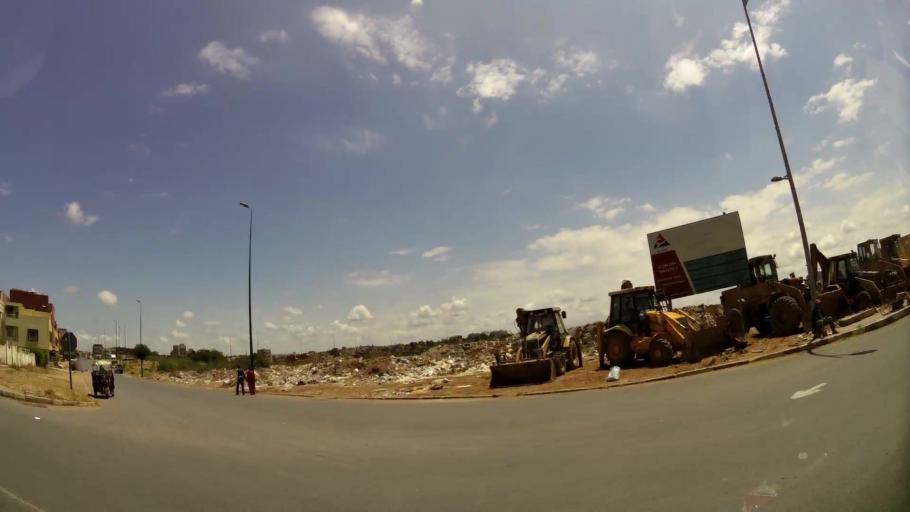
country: MA
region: Gharb-Chrarda-Beni Hssen
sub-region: Kenitra Province
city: Kenitra
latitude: 34.2598
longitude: -6.6120
